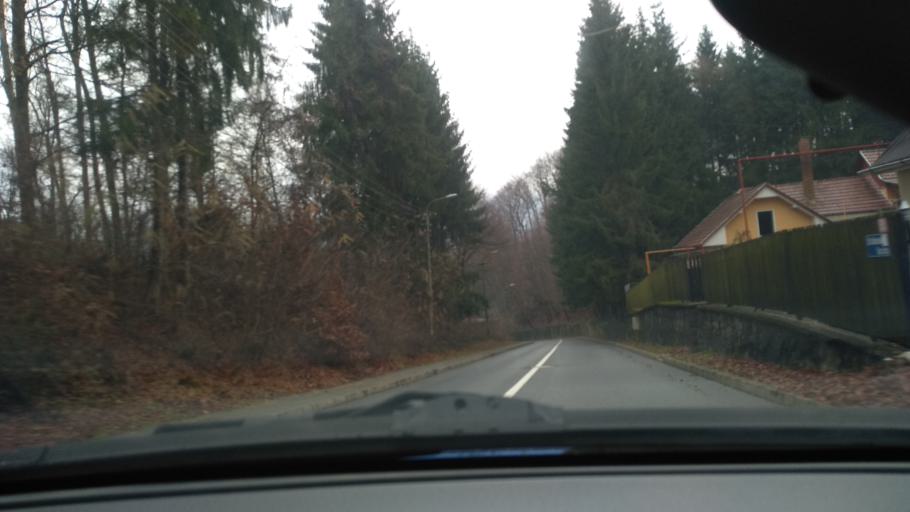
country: RO
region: Mures
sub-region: Oras Sovata
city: Sovata
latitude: 46.5953
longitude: 25.0800
